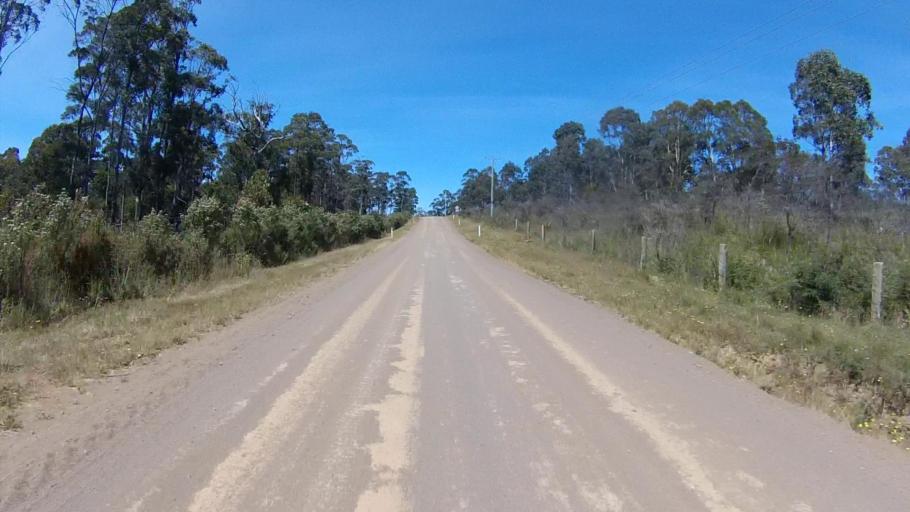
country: AU
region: Tasmania
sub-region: Sorell
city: Sorell
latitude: -42.7311
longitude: 147.7387
